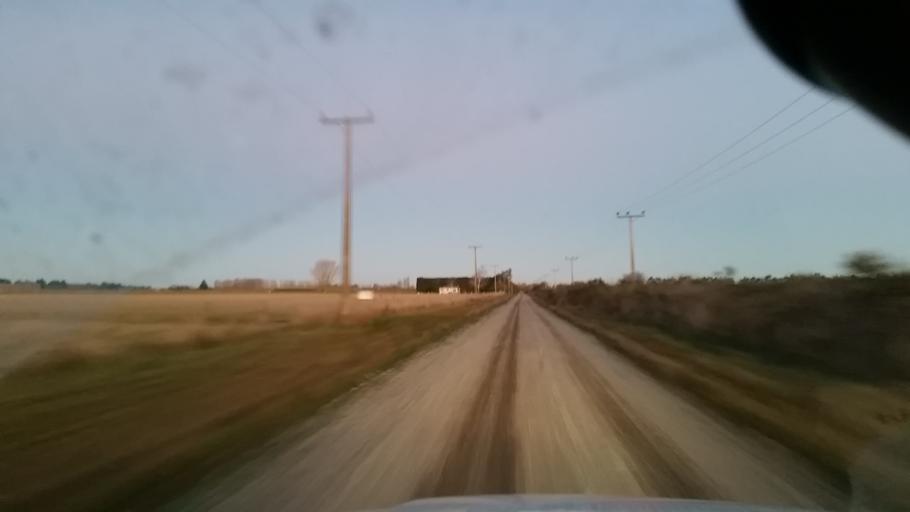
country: NZ
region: Canterbury
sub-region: Ashburton District
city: Tinwald
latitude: -43.9947
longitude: 171.6615
